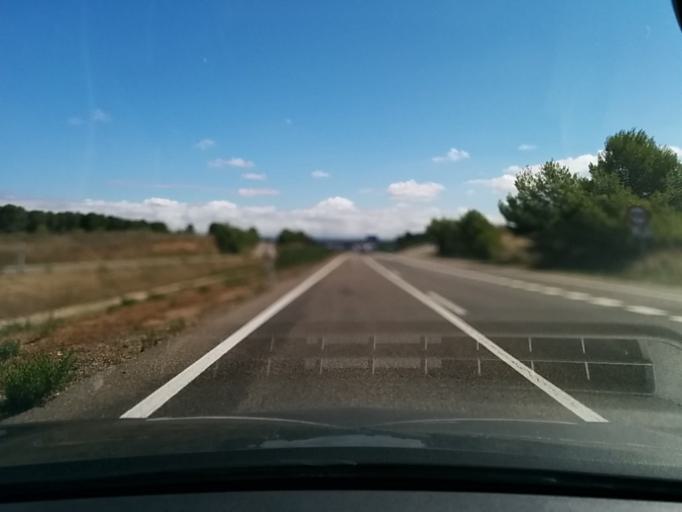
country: ES
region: Aragon
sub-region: Provincia de Huesca
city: Huesca
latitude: 42.1133
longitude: -0.4466
